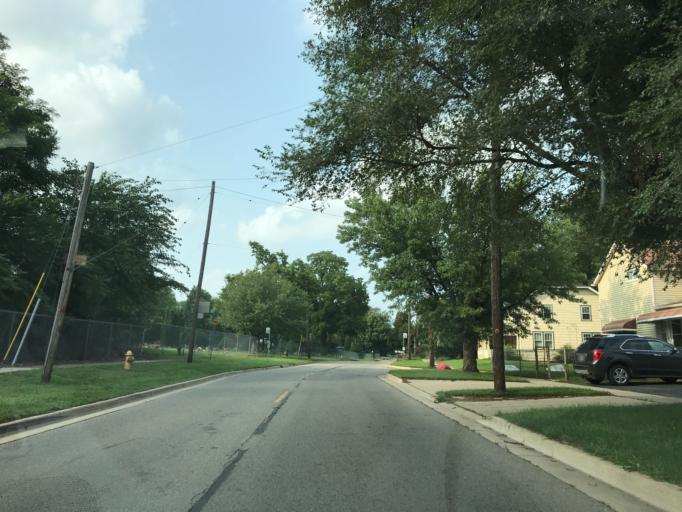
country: US
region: Michigan
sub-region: Washtenaw County
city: Ypsilanti
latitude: 42.2529
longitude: -83.6087
